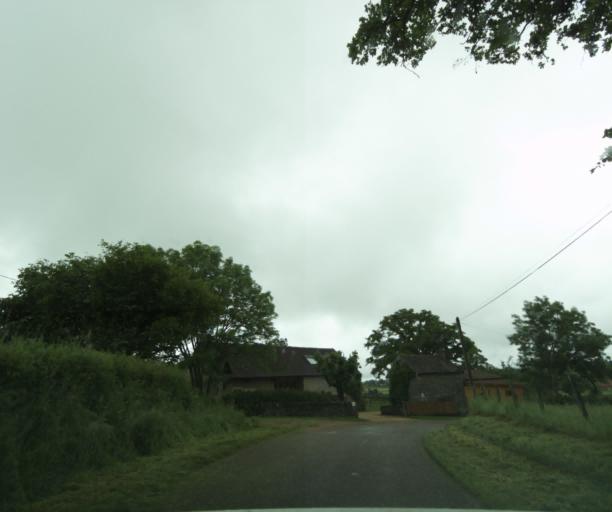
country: FR
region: Bourgogne
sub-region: Departement de Saone-et-Loire
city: Charolles
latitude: 46.4268
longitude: 4.3354
